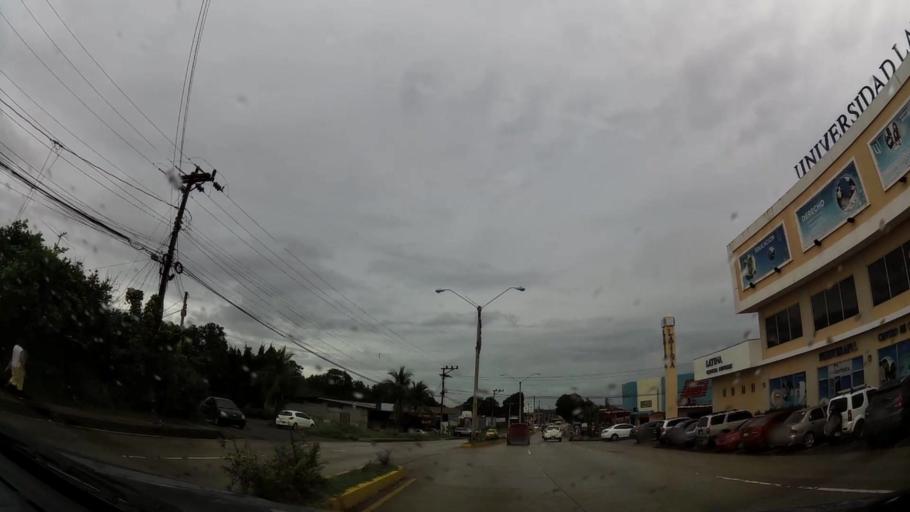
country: PA
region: Veraguas
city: Santiago de Veraguas
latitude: 8.0990
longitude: -80.9717
